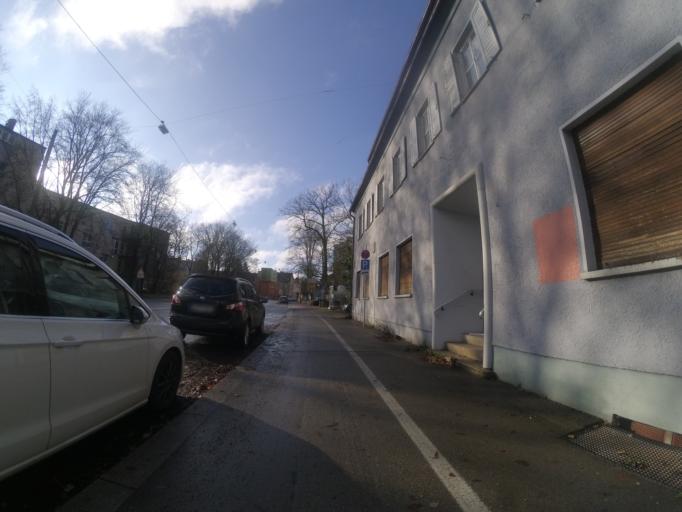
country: DE
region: Bavaria
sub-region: Swabia
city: Neu-Ulm
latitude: 48.3994
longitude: 10.0073
